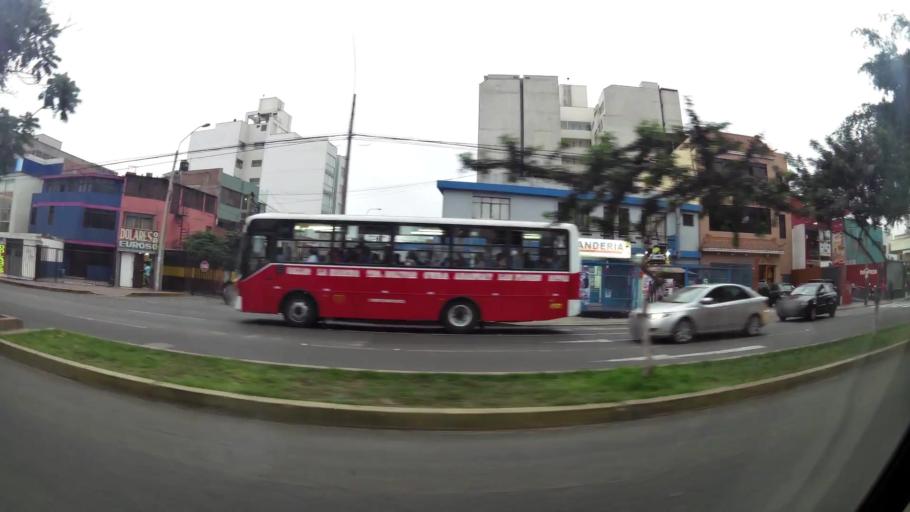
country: PE
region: Lima
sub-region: Lima
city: San Isidro
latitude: -12.0724
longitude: -77.0658
